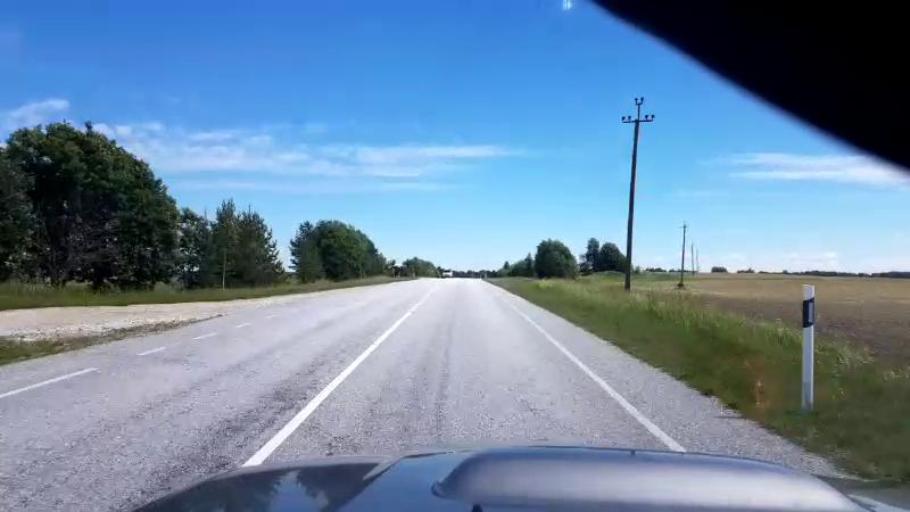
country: EE
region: Laeaene-Virumaa
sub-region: Rakke vald
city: Rakke
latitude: 58.9661
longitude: 26.1464
